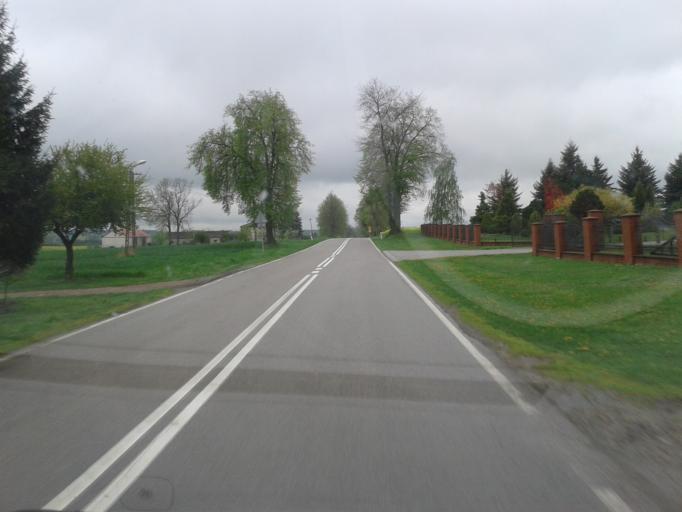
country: PL
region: Lublin Voivodeship
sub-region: Powiat tomaszowski
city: Telatyn
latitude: 50.5378
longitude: 23.9217
